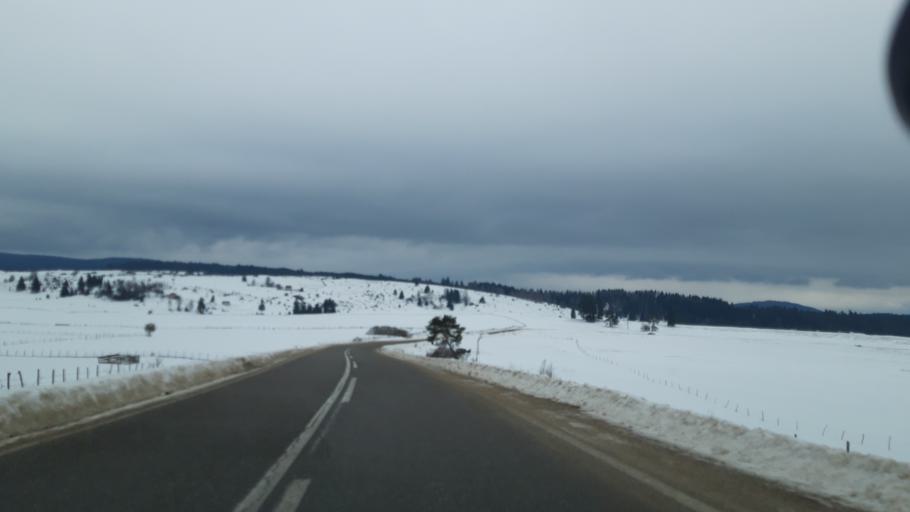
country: BA
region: Republika Srpska
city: Han Pijesak
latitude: 44.0351
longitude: 18.9248
